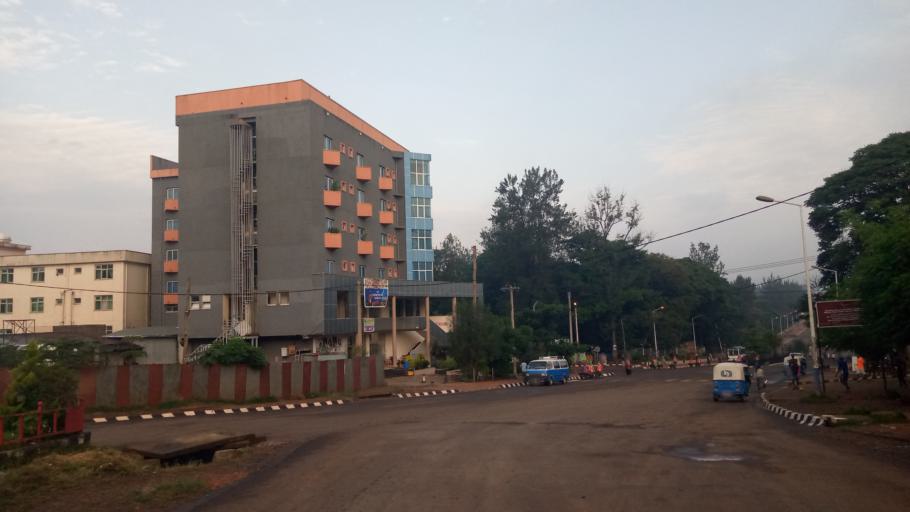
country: ET
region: Oromiya
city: Jima
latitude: 7.6752
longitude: 36.8382
